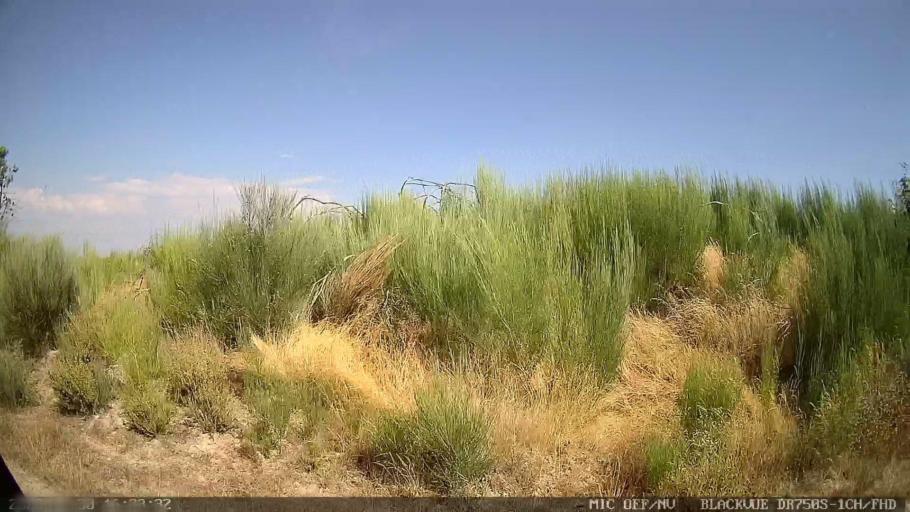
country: PT
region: Vila Real
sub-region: Murca
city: Murca
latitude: 41.3180
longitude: -7.4921
